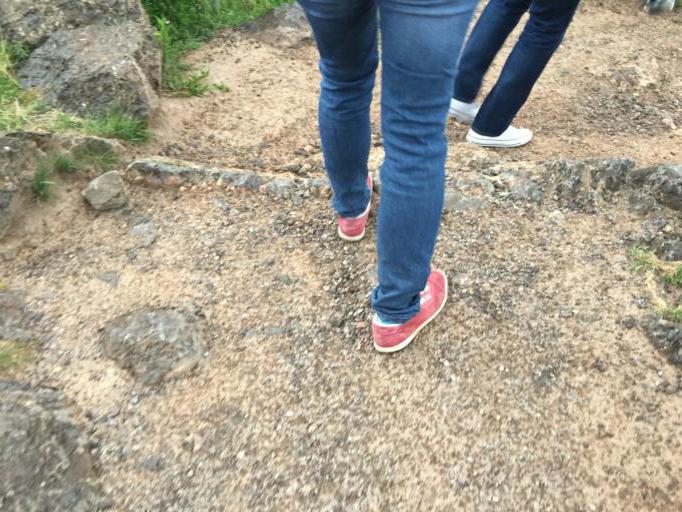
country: PE
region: Cusco
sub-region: Provincia de Cusco
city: Cusco
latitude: -13.5092
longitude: -71.9708
